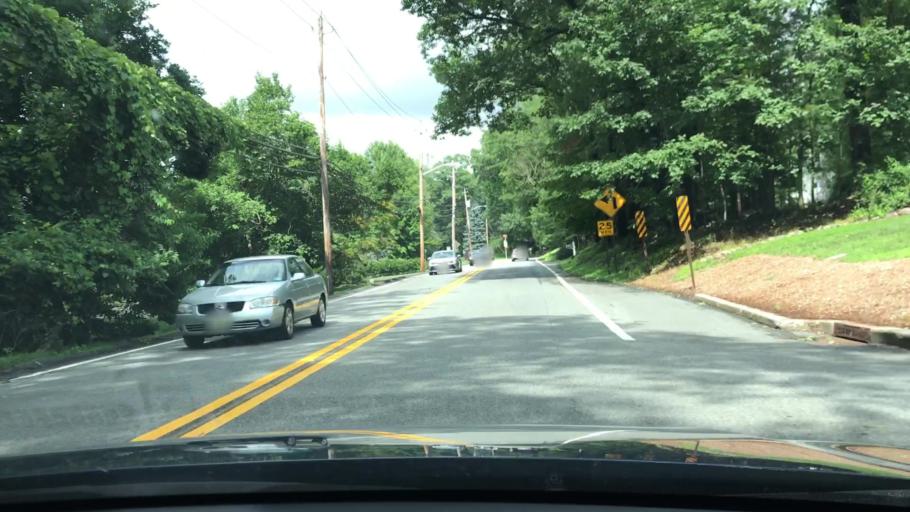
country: US
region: New Jersey
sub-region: Bergen County
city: Wyckoff
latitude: 41.0384
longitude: -74.1646
